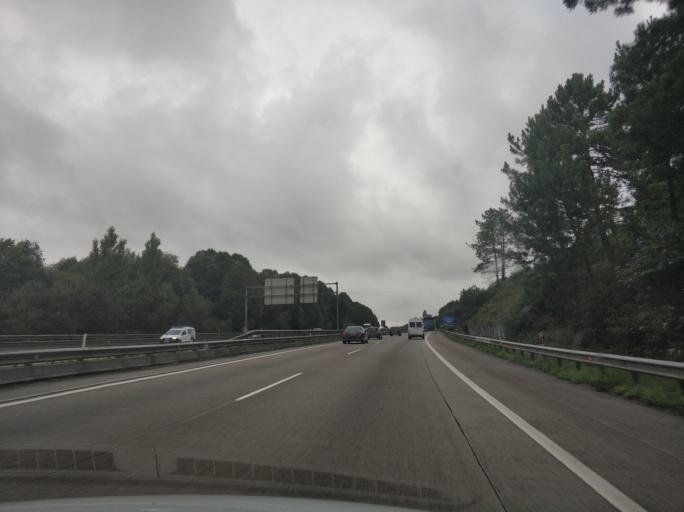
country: ES
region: Asturias
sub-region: Province of Asturias
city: Corvera de Asturias
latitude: 43.5056
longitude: -5.8051
